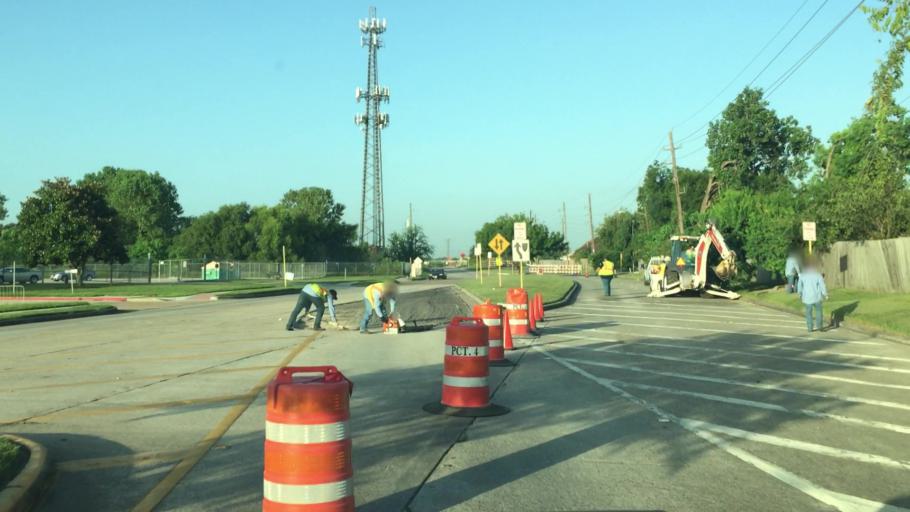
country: US
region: Texas
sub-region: Harris County
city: Hudson
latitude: 29.9464
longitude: -95.4722
